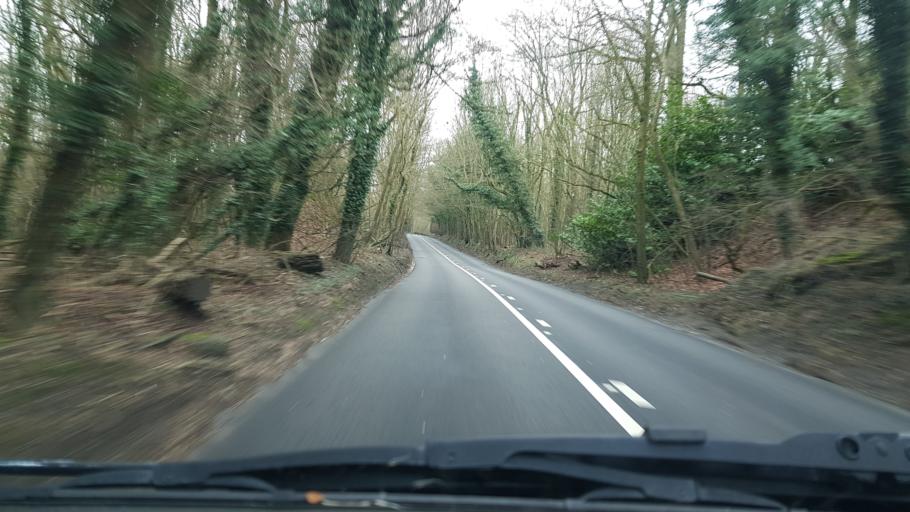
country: GB
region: England
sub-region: Wiltshire
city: Burbage
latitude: 51.3757
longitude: -1.6832
